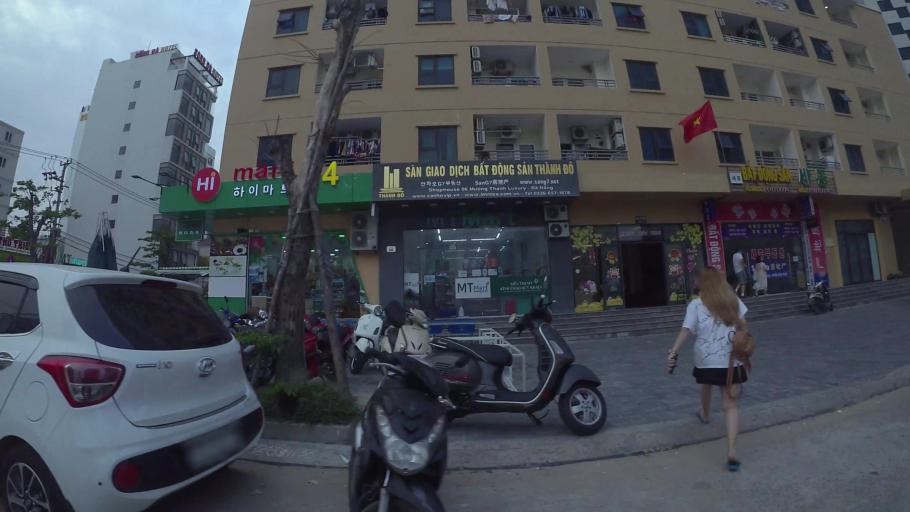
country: VN
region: Da Nang
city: Son Tra
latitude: 16.0530
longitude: 108.2468
